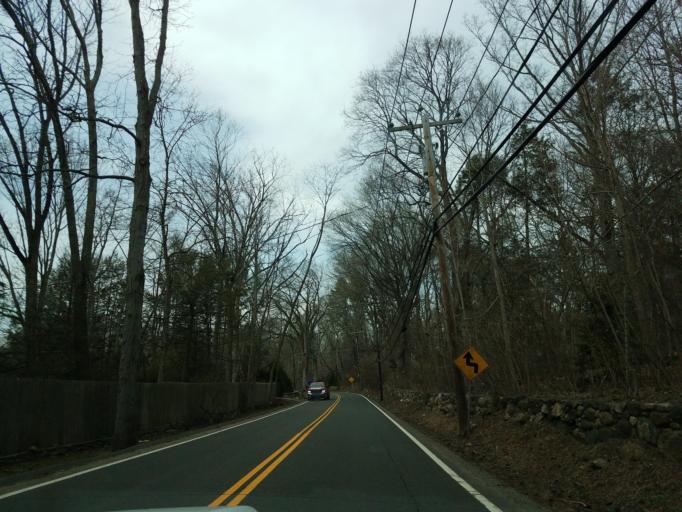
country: US
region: Connecticut
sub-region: Fairfield County
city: Glenville
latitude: 41.0689
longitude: -73.6394
